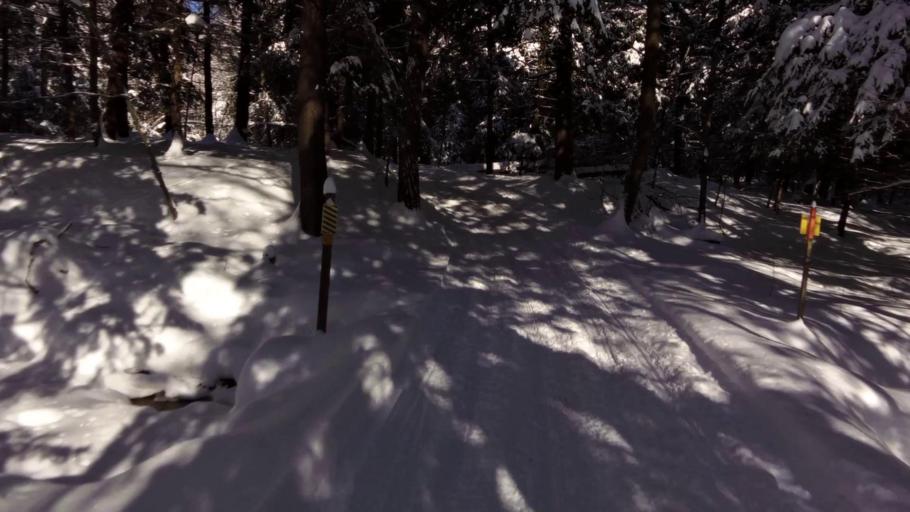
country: US
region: New York
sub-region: Chautauqua County
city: Fredonia
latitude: 42.3585
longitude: -79.1788
